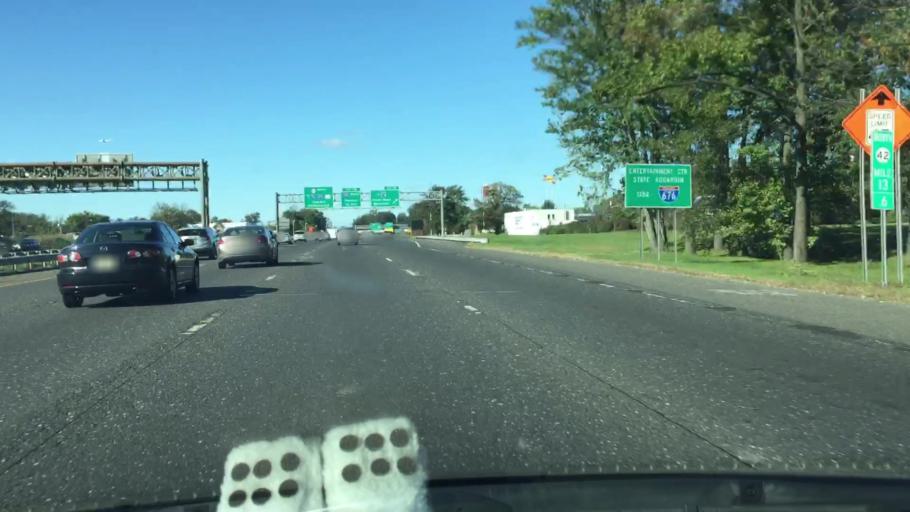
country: US
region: New Jersey
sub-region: Camden County
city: Bellmawr
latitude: 39.8602
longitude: -75.0995
